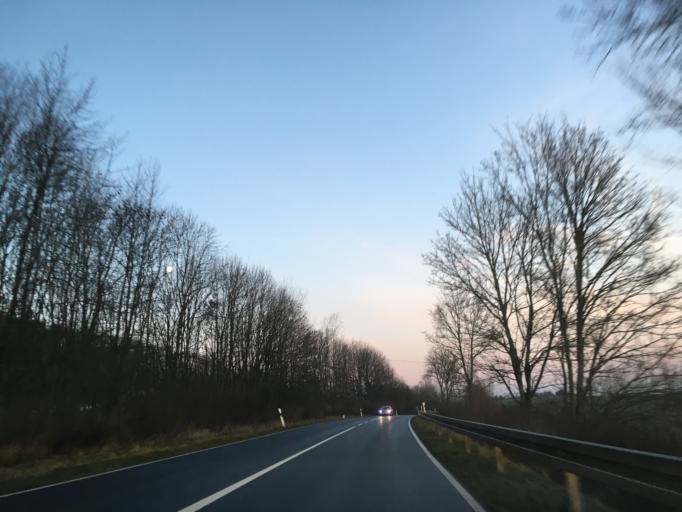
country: DE
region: Hesse
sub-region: Regierungsbezirk Kassel
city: Hofbieber
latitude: 50.5897
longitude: 9.8499
